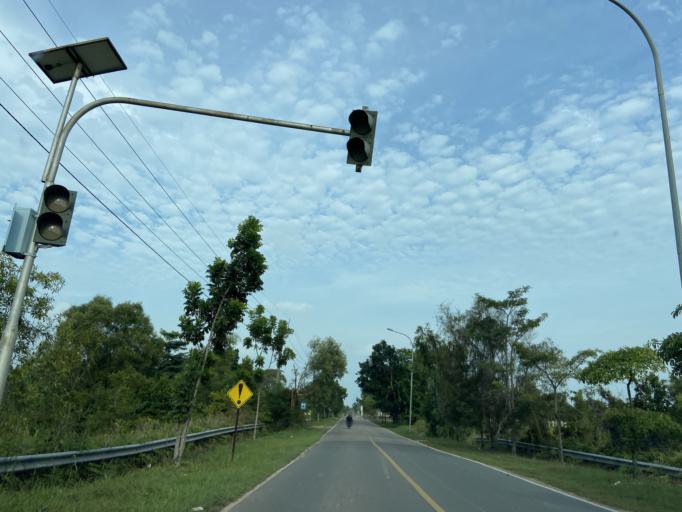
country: ID
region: Riau Islands
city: Tanjungpinang
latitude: 0.9516
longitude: 104.0738
